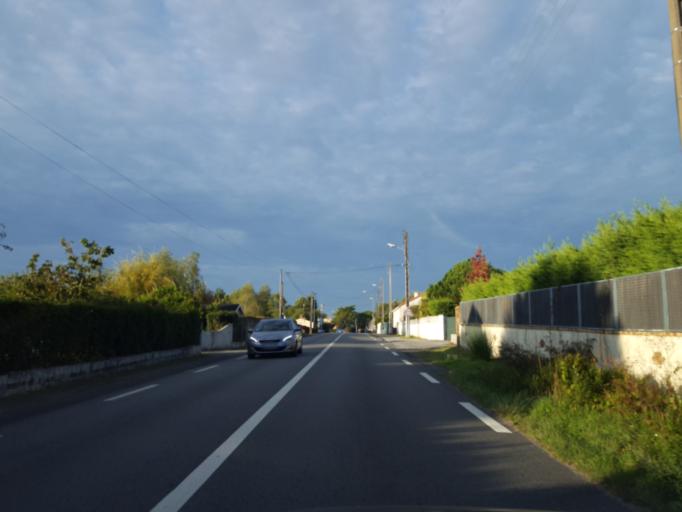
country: FR
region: Pays de la Loire
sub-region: Departement de la Loire-Atlantique
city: Basse-Goulaine
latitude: 47.1948
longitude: -1.4607
